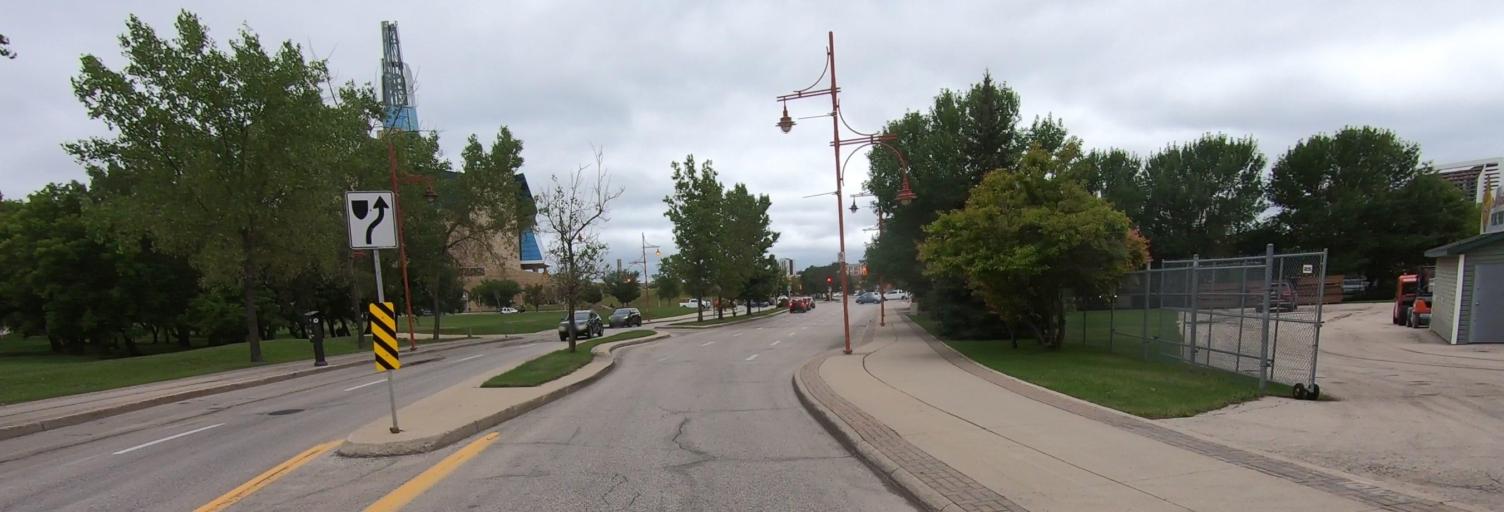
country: CA
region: Manitoba
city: Winnipeg
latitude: 49.8934
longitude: -97.1317
